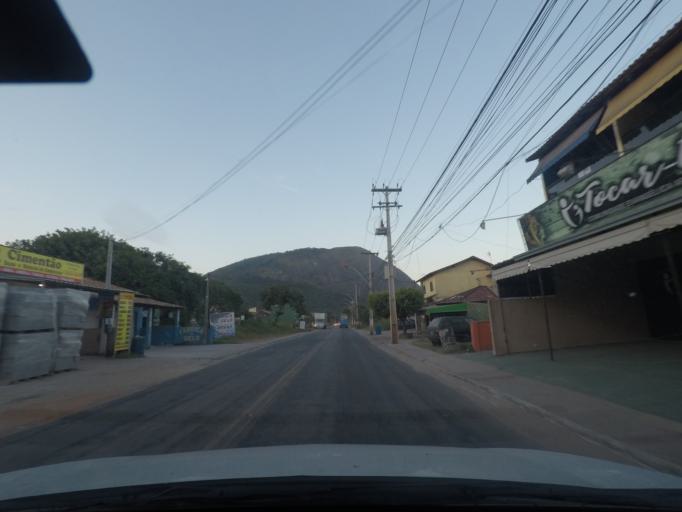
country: BR
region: Rio de Janeiro
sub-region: Marica
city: Marica
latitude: -22.9530
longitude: -42.9623
